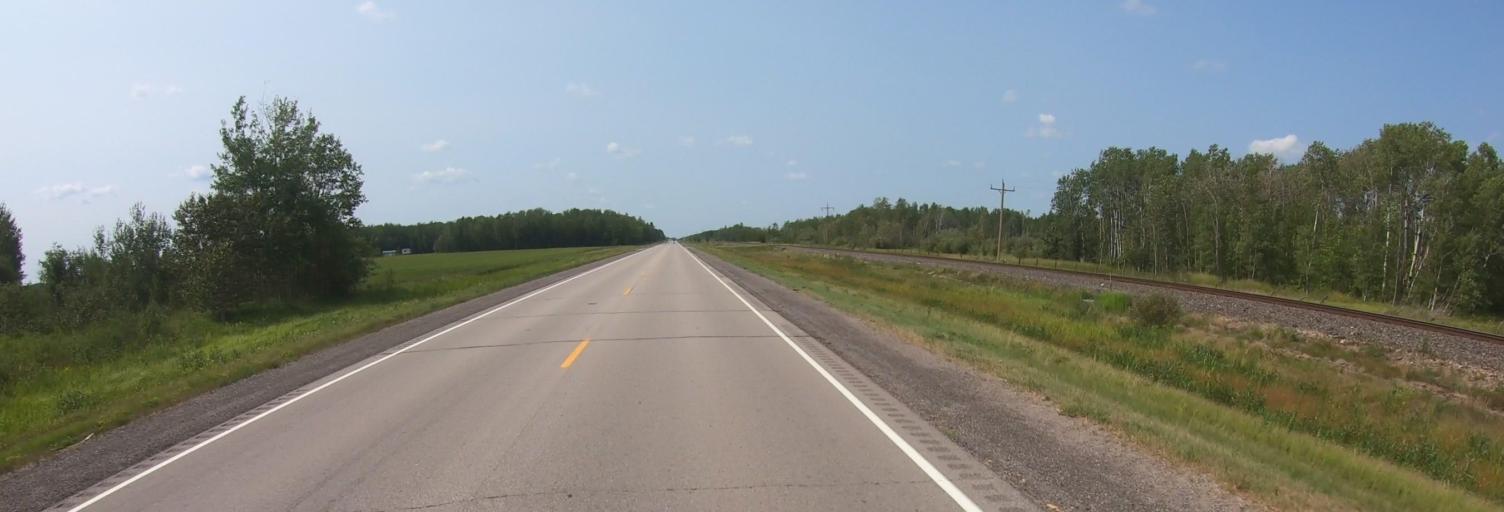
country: US
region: Minnesota
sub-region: Lake of the Woods County
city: Baudette
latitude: 48.7238
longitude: -94.7666
